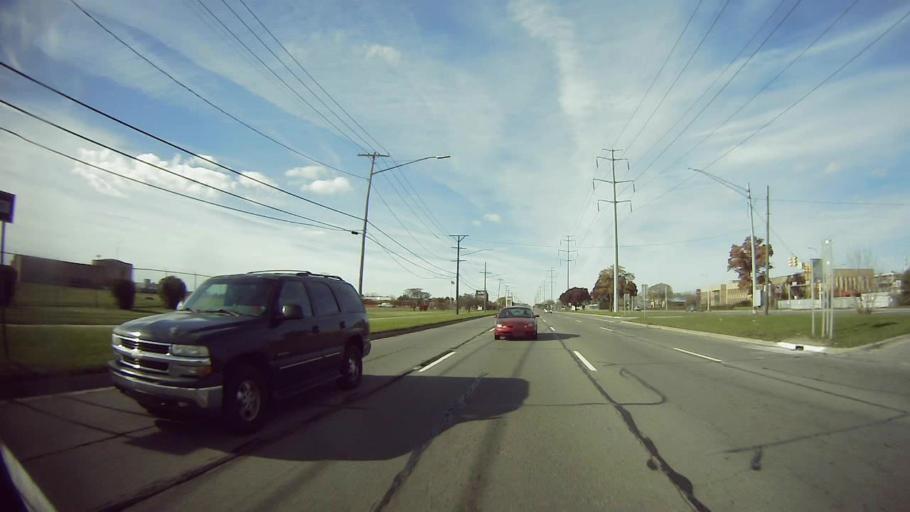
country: US
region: Michigan
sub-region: Macomb County
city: Warren
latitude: 42.4485
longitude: -83.0120
